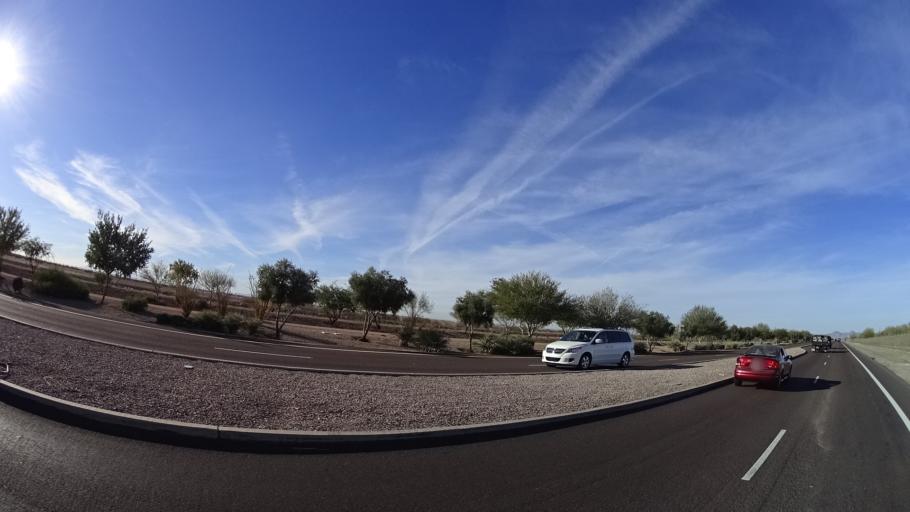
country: US
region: Arizona
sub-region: Maricopa County
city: Queen Creek
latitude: 33.2981
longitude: -111.6350
